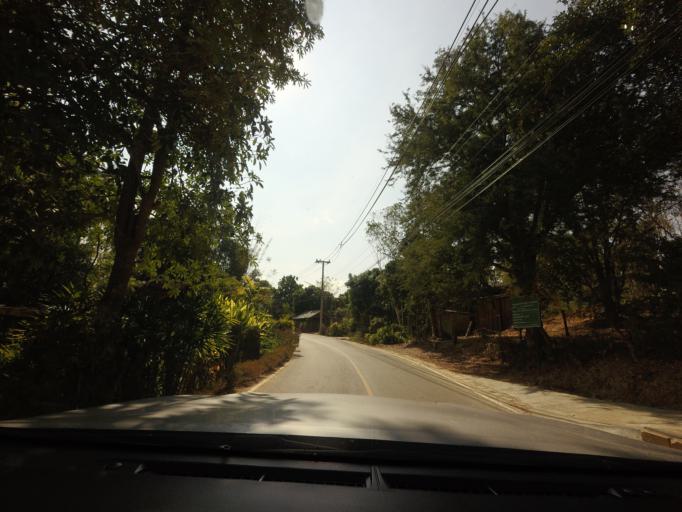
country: TH
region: Mae Hong Son
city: Wiang Nuea
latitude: 19.3994
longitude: 98.4427
